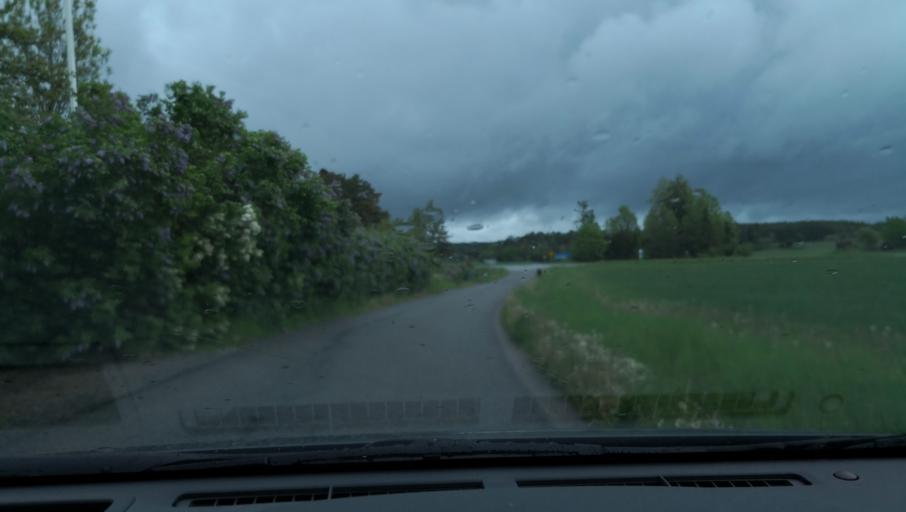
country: SE
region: Uppsala
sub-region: Enkopings Kommun
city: Orsundsbro
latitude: 59.8106
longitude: 17.3827
